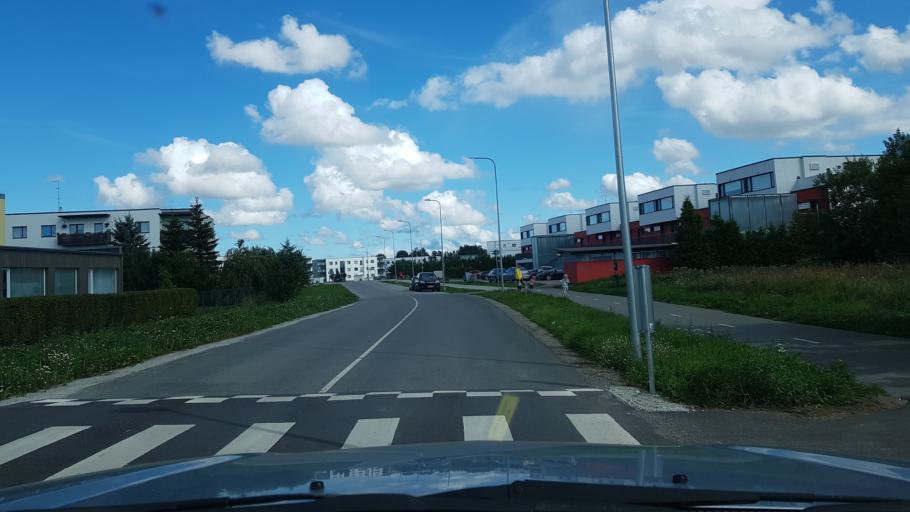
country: EE
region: Harju
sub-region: Tallinna linn
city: Tallinn
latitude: 59.3934
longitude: 24.8023
